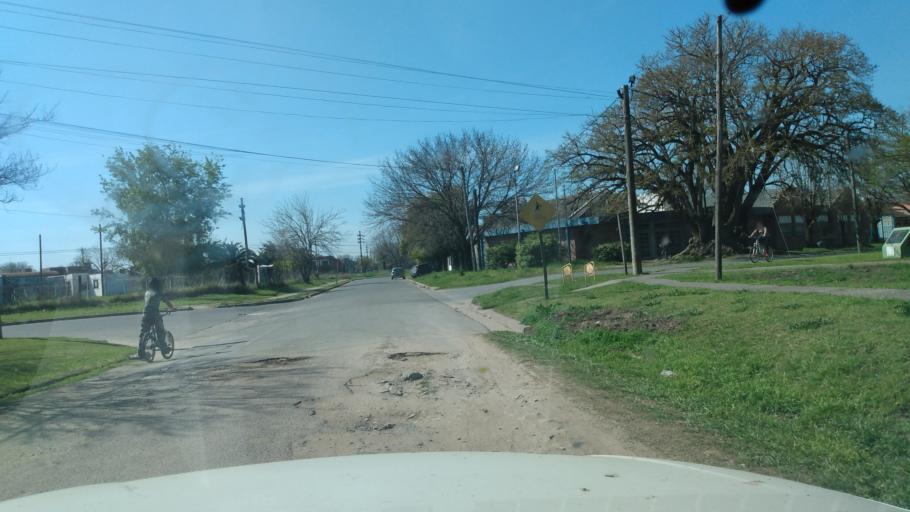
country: AR
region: Buenos Aires
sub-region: Partido de Lujan
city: Lujan
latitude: -34.5777
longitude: -59.1015
